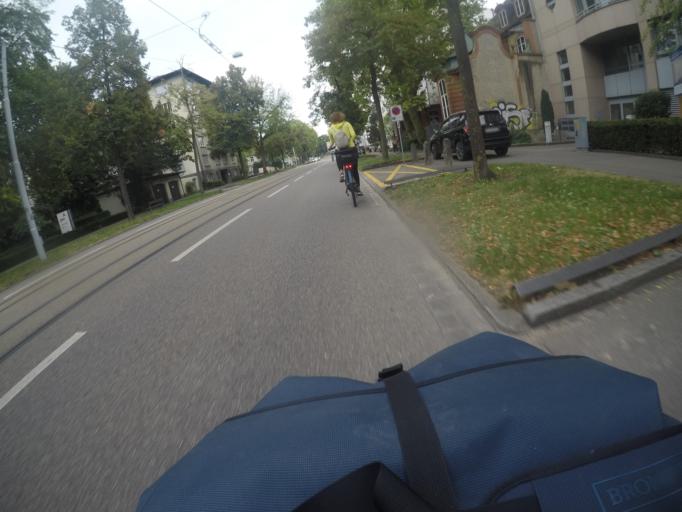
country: CH
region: Basel-City
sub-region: Basel-Stadt
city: Basel
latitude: 47.5498
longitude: 7.5966
